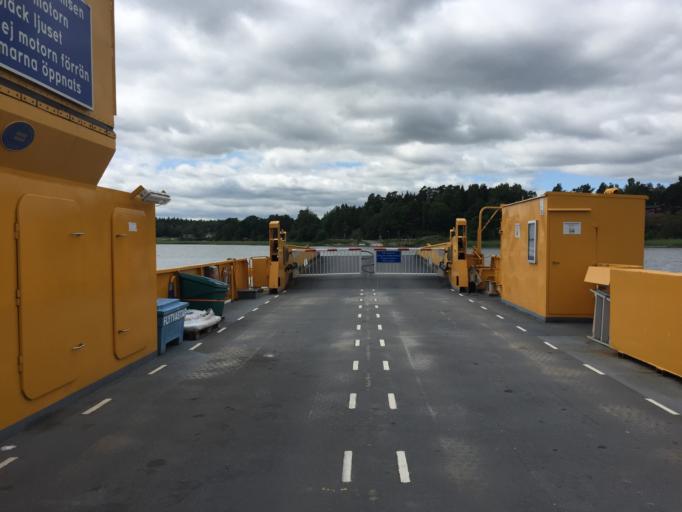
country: SE
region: Soedermanland
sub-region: Trosa Kommun
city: Trosa
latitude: 58.9710
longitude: 17.7073
